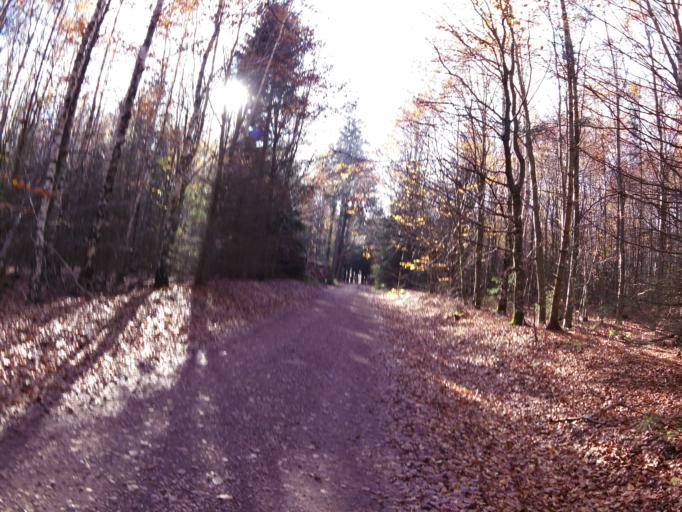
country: DE
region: Thuringia
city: Ruhla
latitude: 50.9021
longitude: 10.3382
